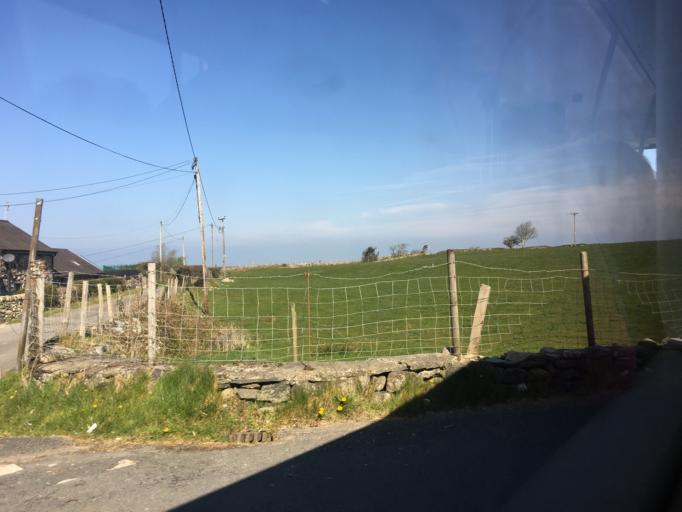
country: GB
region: Wales
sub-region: Gwynedd
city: Llanwnda
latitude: 53.0345
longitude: -4.2868
